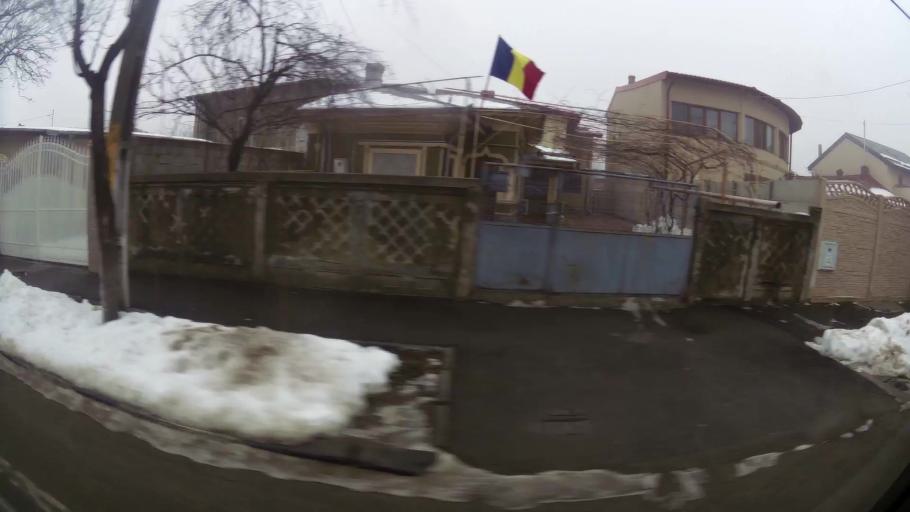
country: RO
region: Ilfov
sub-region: Comuna Chiajna
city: Chiajna
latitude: 44.4601
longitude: 25.9809
